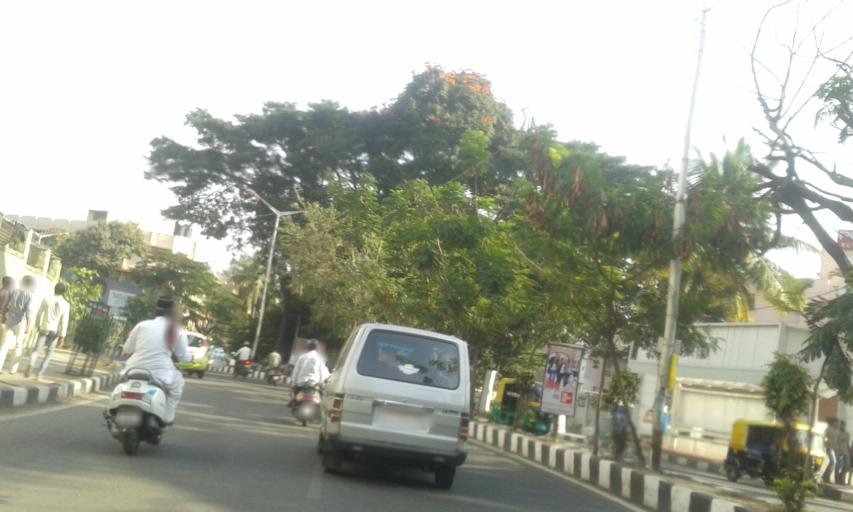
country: IN
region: Karnataka
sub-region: Bangalore Urban
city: Bangalore
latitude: 12.9282
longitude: 77.5876
